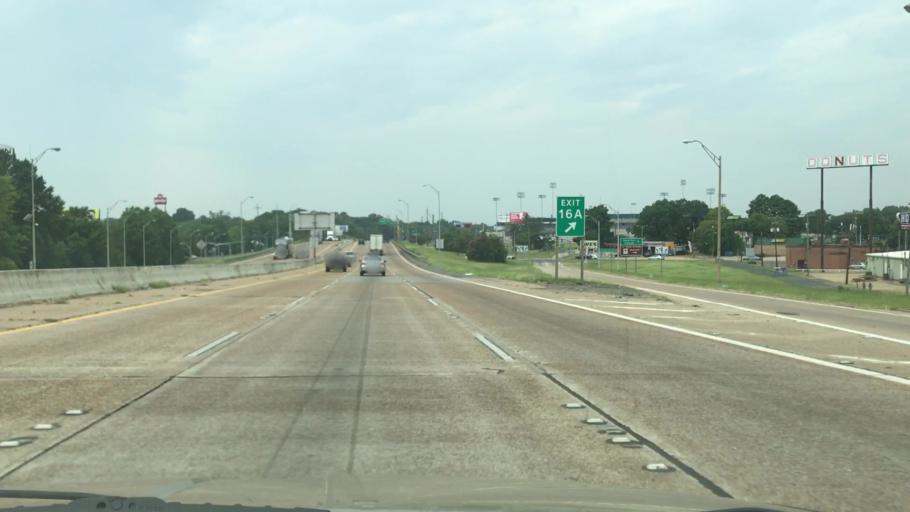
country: US
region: Louisiana
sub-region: Caddo Parish
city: Shreveport
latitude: 32.4809
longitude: -93.7776
